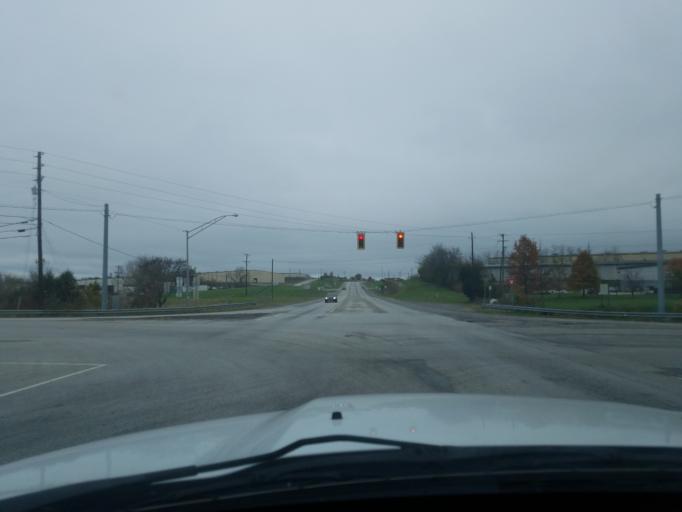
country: US
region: Kentucky
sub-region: Washington County
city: Springfield
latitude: 37.6906
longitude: -85.2326
